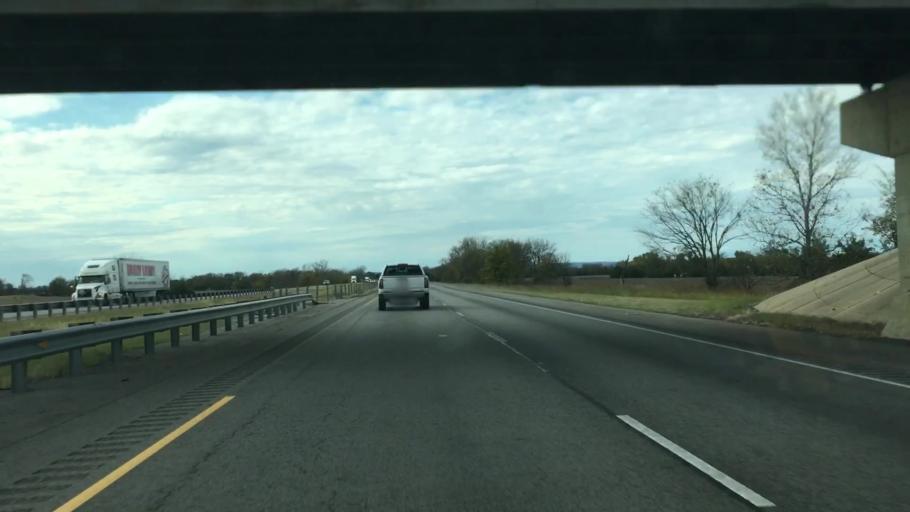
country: US
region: Arkansas
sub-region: Conway County
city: Morrilton
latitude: 35.1914
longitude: -92.7880
